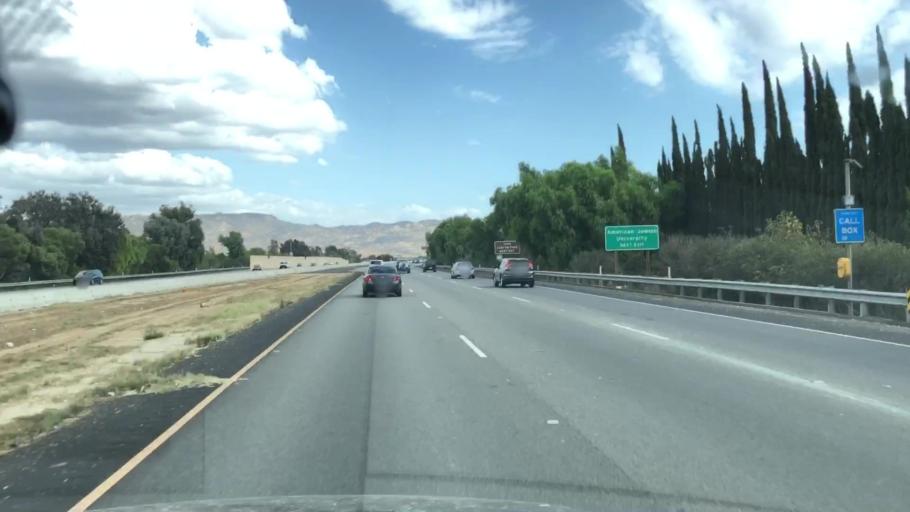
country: US
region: California
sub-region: Ventura County
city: Santa Susana
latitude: 34.2822
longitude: -118.7255
